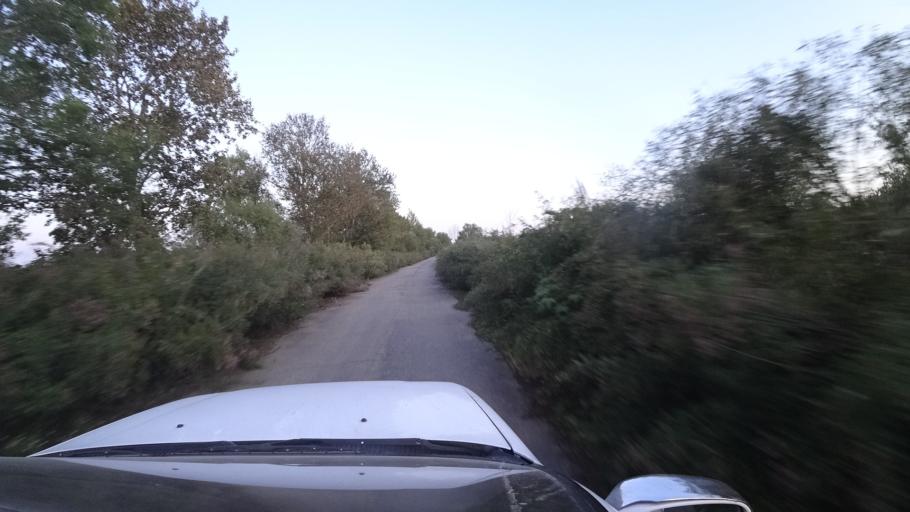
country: RU
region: Primorskiy
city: Dal'nerechensk
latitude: 45.9472
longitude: 133.7635
